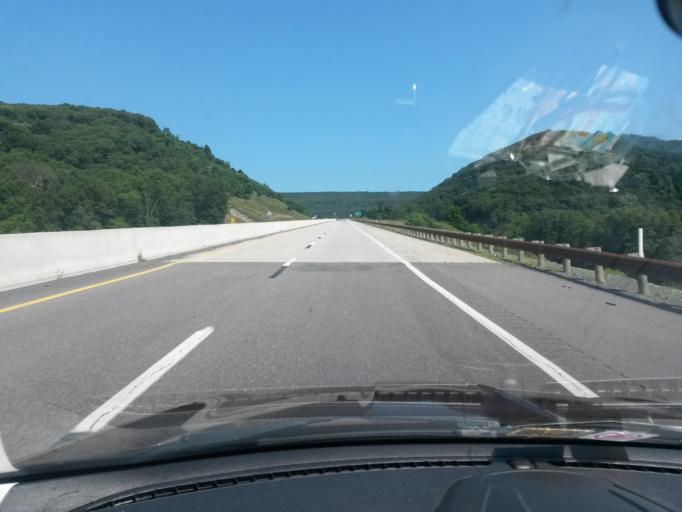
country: US
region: West Virginia
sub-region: Grant County
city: Petersburg
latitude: 39.1560
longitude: -79.1357
